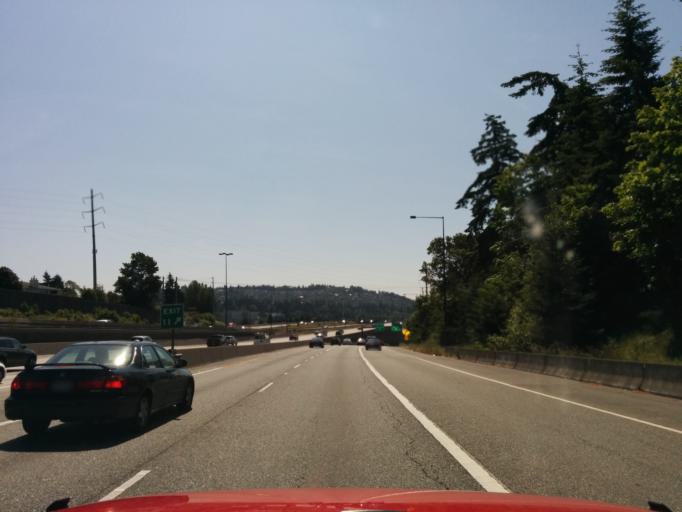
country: US
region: Washington
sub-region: King County
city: Newport
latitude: 47.5846
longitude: -122.1778
